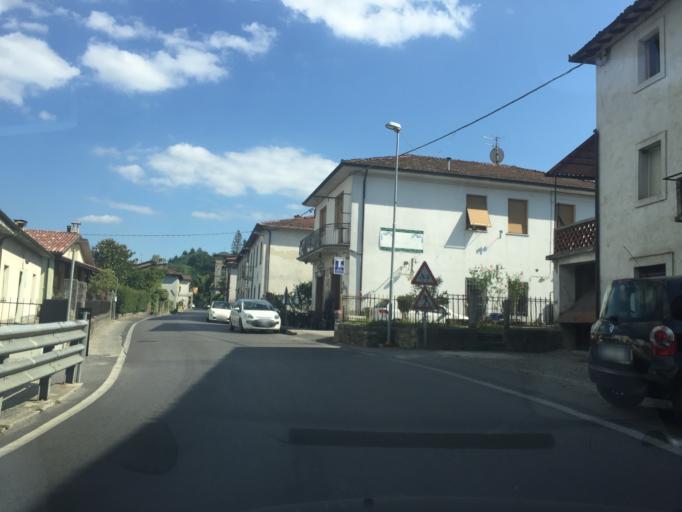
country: IT
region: Tuscany
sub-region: Provincia di Lucca
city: Villa Collemandina
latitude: 44.1360
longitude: 10.3692
